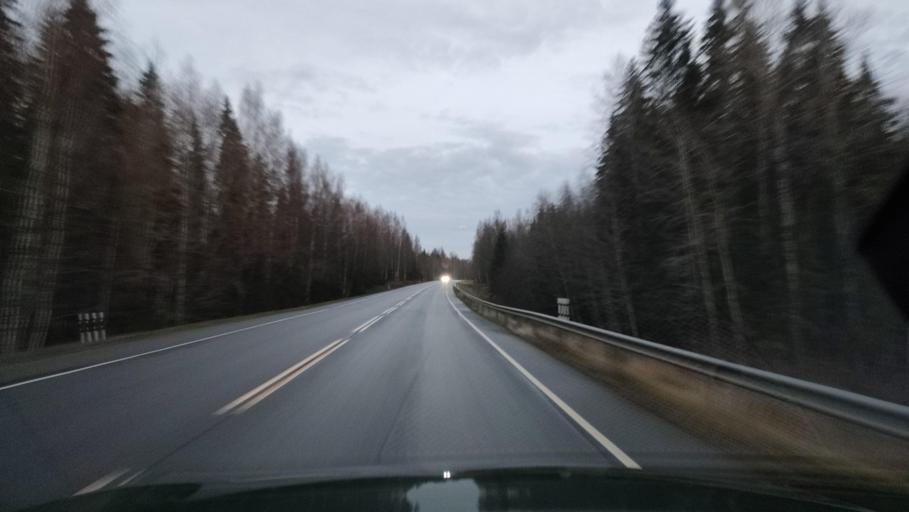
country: FI
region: Ostrobothnia
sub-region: Vaasa
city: Ristinummi
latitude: 62.9803
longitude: 21.7690
